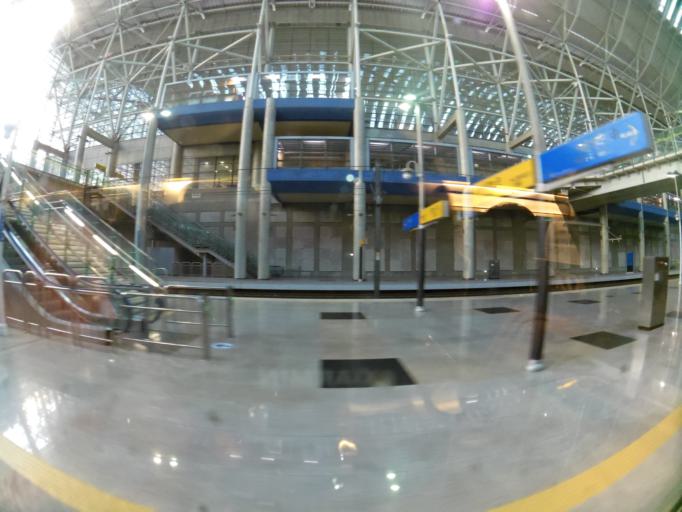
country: KR
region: Gyeonggi-do
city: Anyang-si
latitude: 37.4153
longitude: 126.8839
